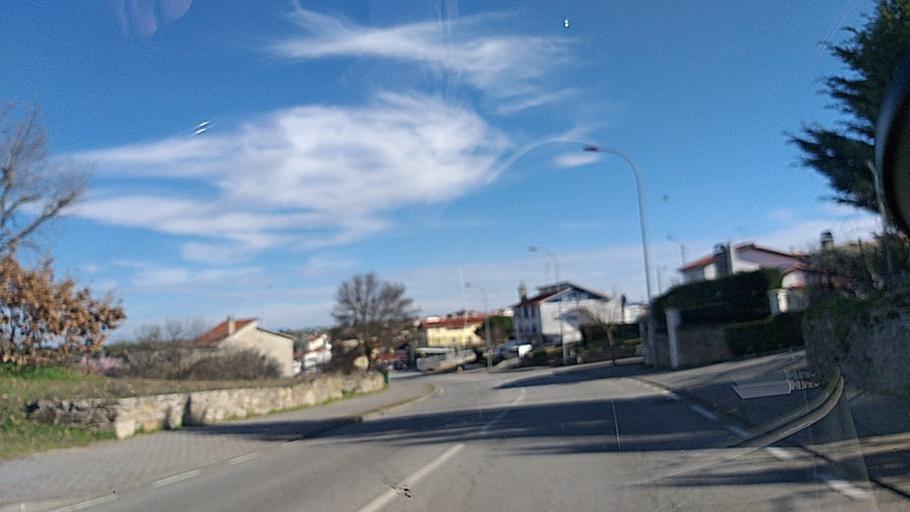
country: ES
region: Castille and Leon
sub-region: Provincia de Salamanca
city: Fuentes de Onoro
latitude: 40.6163
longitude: -6.8405
